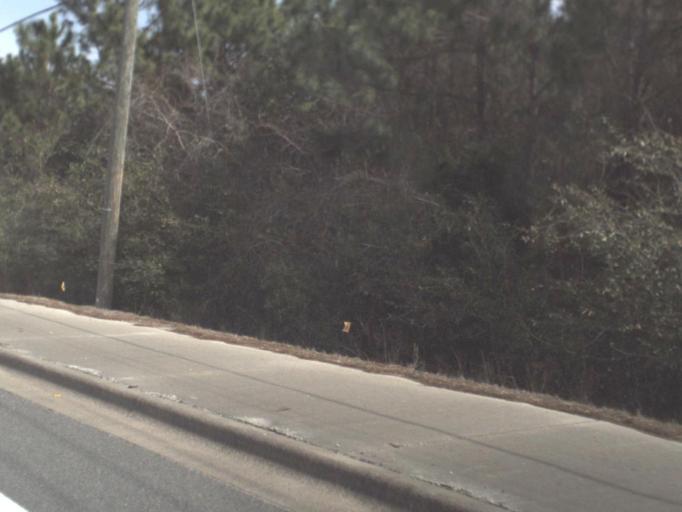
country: US
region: Florida
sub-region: Bay County
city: Pretty Bayou
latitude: 30.1857
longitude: -85.7208
